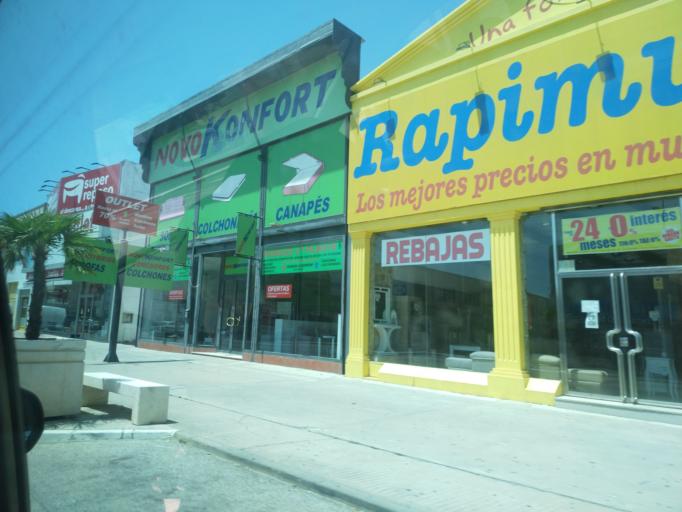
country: ES
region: Andalusia
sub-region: Provincia de Cadiz
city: Chiclana de la Frontera
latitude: 36.4297
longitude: -6.1483
